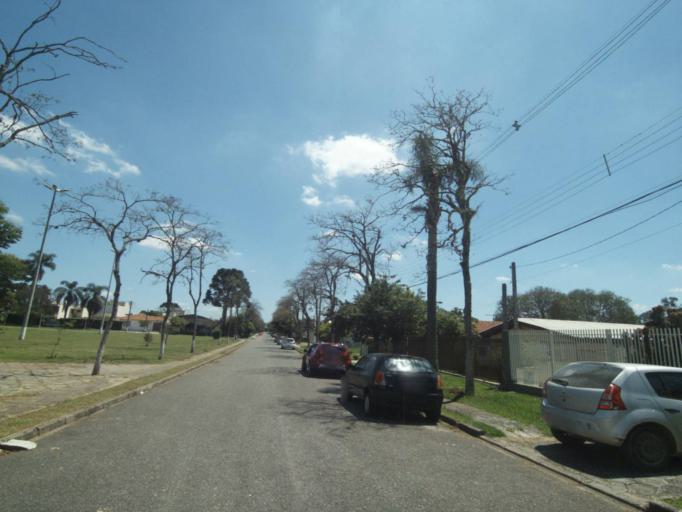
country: BR
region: Parana
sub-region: Curitiba
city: Curitiba
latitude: -25.3999
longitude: -49.2287
